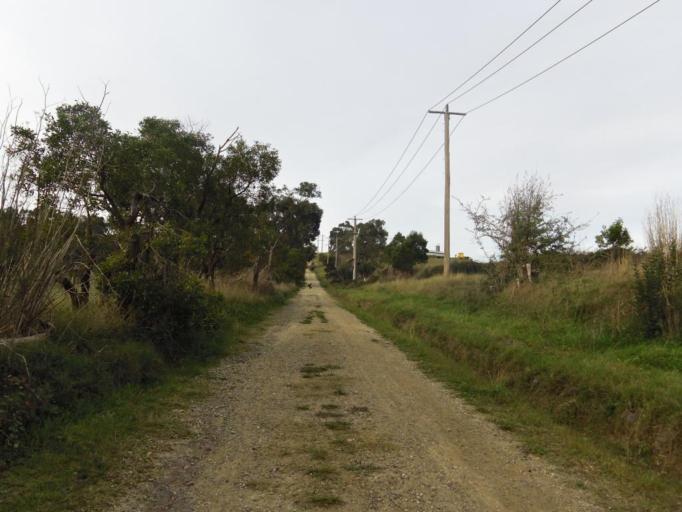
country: AU
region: Victoria
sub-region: Yarra Ranges
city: Belgrave South
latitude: -37.9227
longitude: 145.3224
